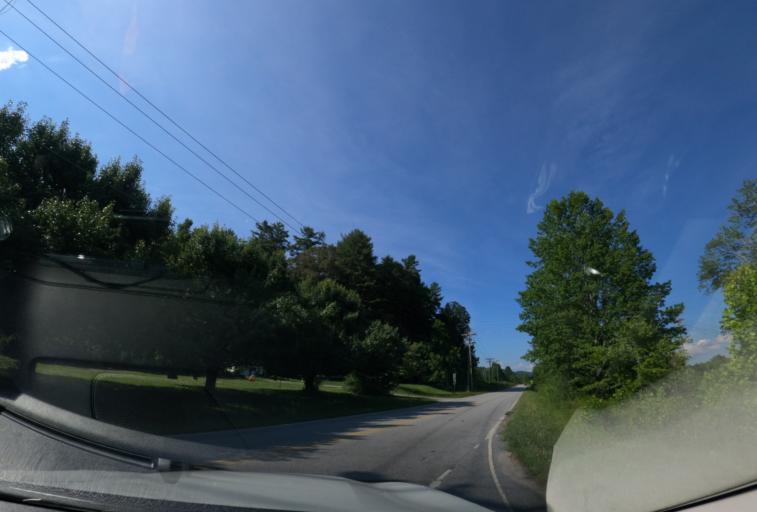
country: US
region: North Carolina
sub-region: Transylvania County
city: Brevard
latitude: 35.2534
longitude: -82.6836
